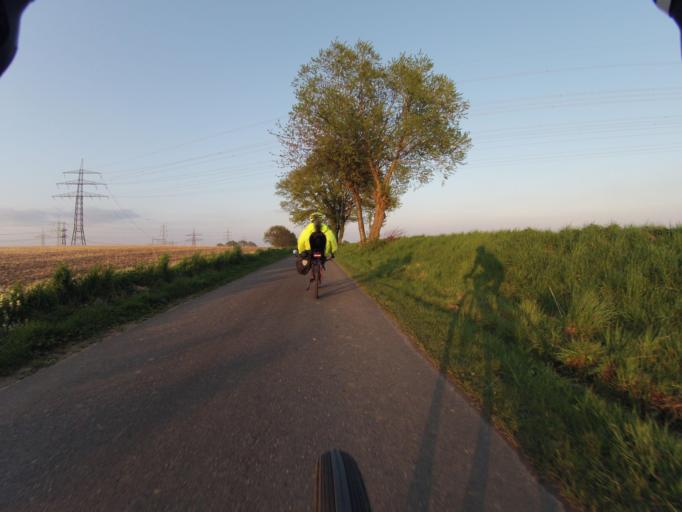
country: DE
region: North Rhine-Westphalia
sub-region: Regierungsbezirk Munster
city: Lotte
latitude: 52.2738
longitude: 7.8827
